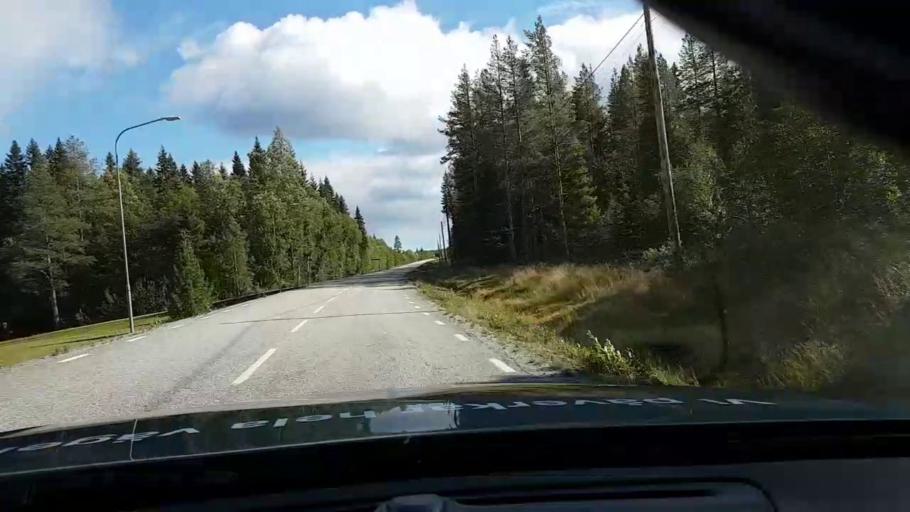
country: SE
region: Vaesterbotten
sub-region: Asele Kommun
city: Asele
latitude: 63.7829
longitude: 17.6590
